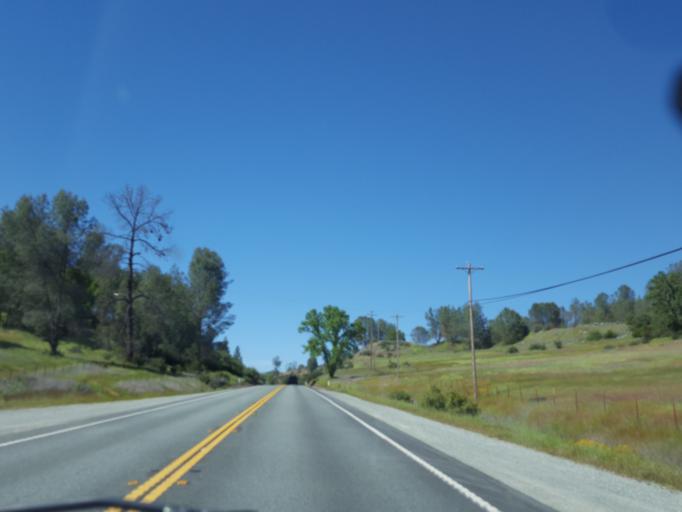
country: US
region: California
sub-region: Calaveras County
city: San Andreas
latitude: 38.2095
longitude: -120.6972
